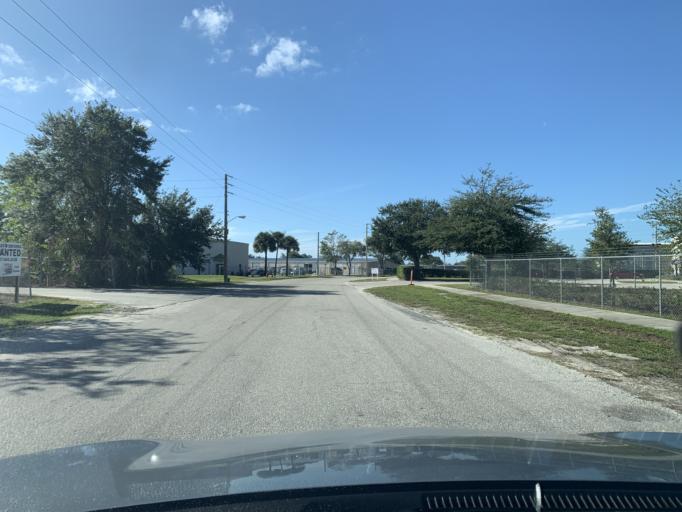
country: US
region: Florida
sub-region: Orange County
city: Lockhart
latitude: 28.6310
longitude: -81.4655
